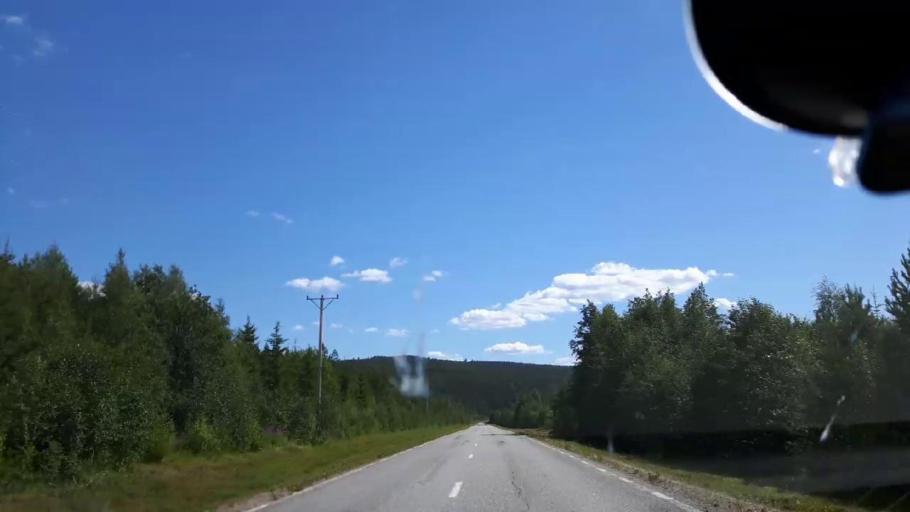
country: SE
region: Vaesternorrland
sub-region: Ange Kommun
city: Fransta
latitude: 62.7477
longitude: 16.3215
